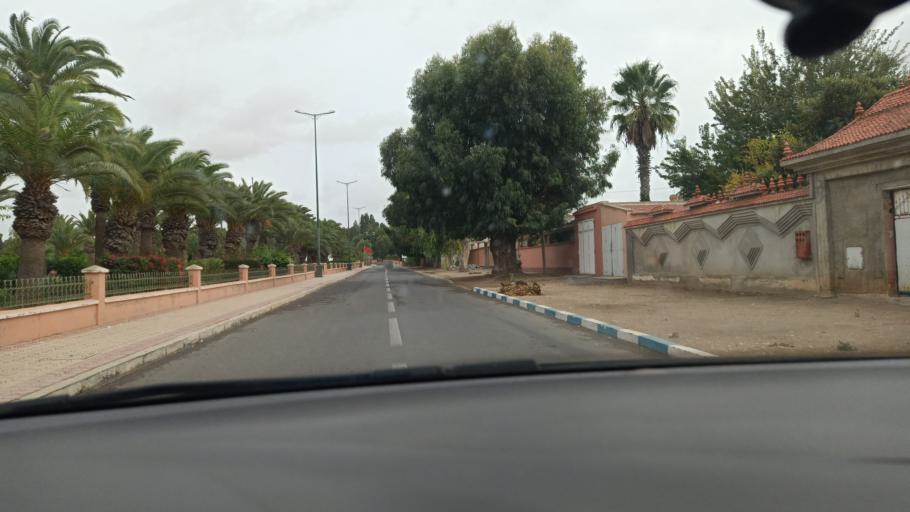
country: MA
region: Doukkala-Abda
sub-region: Safi
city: Youssoufia
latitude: 32.2450
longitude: -8.5300
